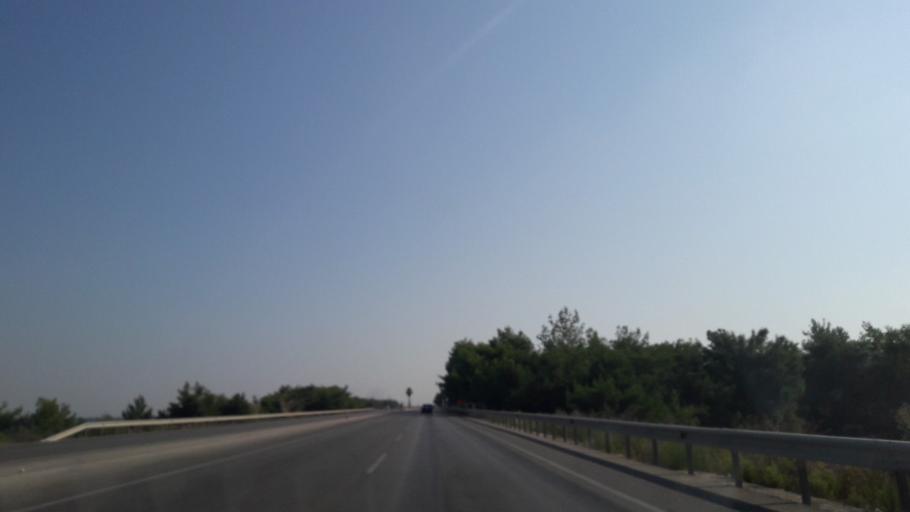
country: TR
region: Adana
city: Yuregir
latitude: 37.0884
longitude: 35.4889
